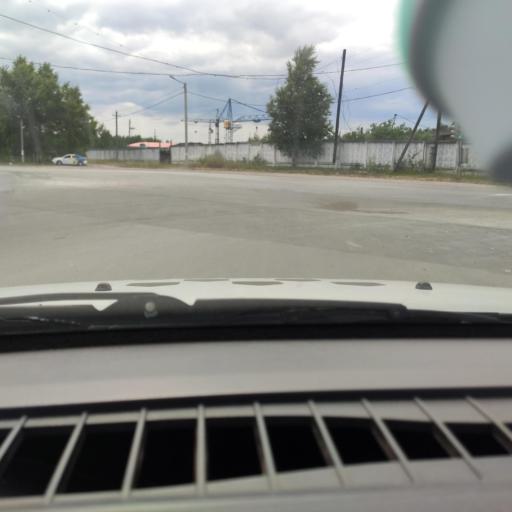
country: RU
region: Perm
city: Solikamsk
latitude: 59.6617
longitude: 56.7591
